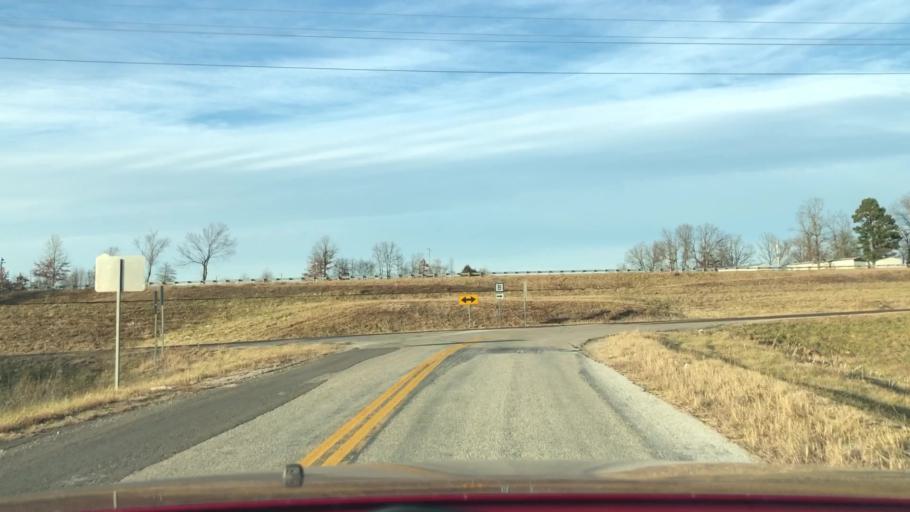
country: US
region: Missouri
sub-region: Wright County
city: Mansfield
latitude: 37.1124
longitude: -92.6295
